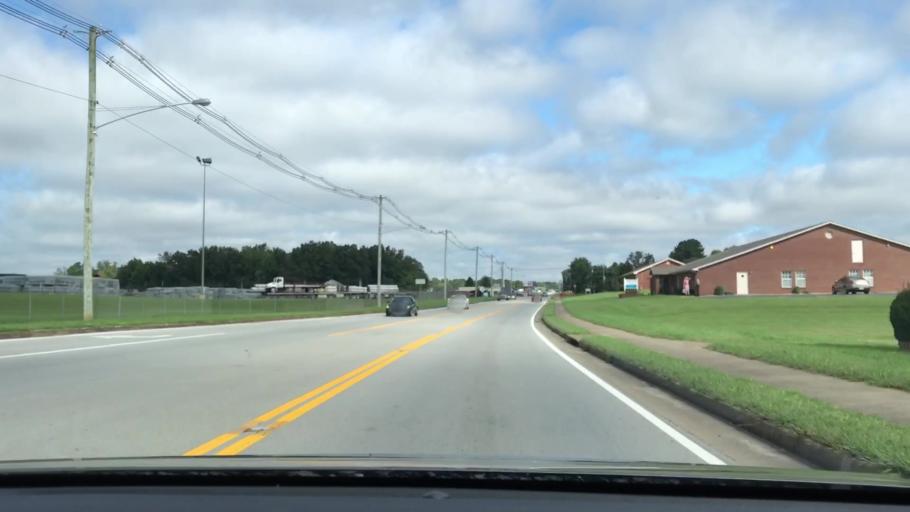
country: US
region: Kentucky
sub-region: Russell County
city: Jamestown
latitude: 37.0107
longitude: -85.0753
